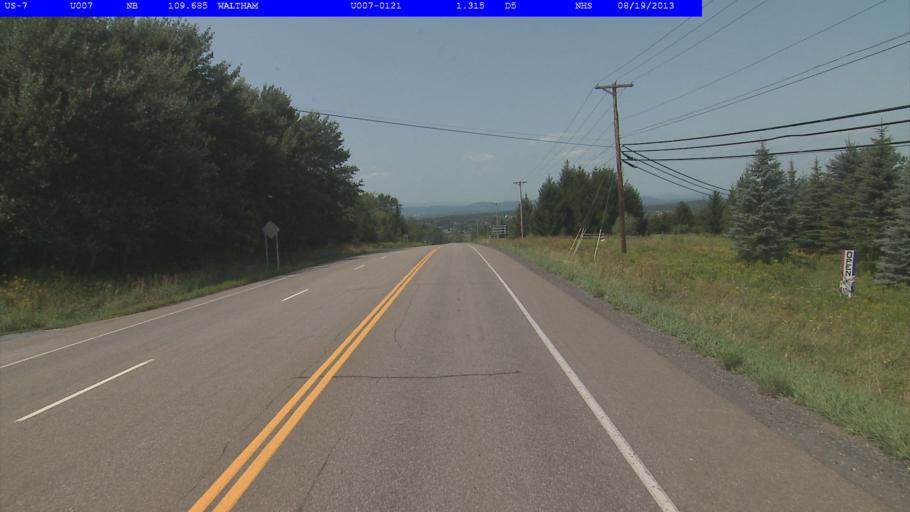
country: US
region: Vermont
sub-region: Addison County
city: Vergennes
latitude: 44.1604
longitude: -73.2295
